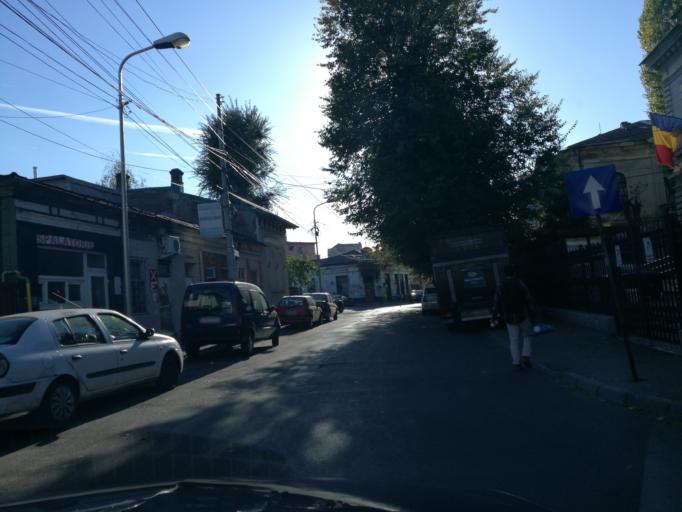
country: RO
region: Bucuresti
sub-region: Municipiul Bucuresti
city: Bucharest
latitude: 44.4438
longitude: 26.1078
